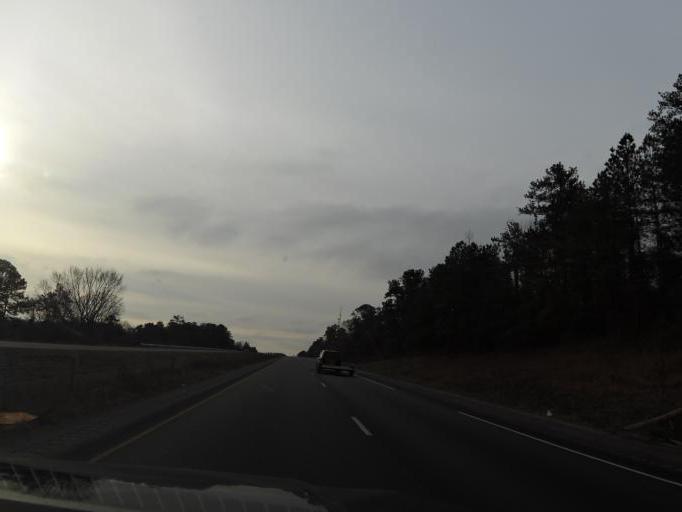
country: US
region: Alabama
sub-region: Autauga County
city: Pine Level
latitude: 32.6358
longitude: -86.4922
